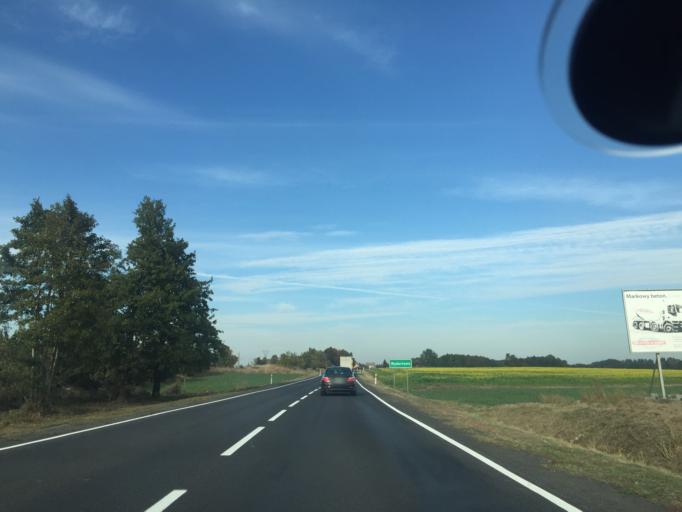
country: PL
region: Greater Poland Voivodeship
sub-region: Powiat gnieznienski
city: Trzemeszno
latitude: 52.6001
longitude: 17.8954
